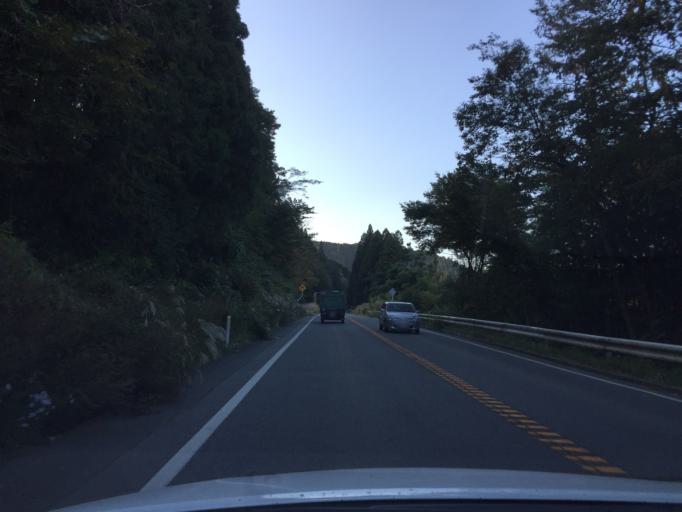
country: JP
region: Fukushima
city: Ishikawa
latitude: 37.1509
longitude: 140.6627
